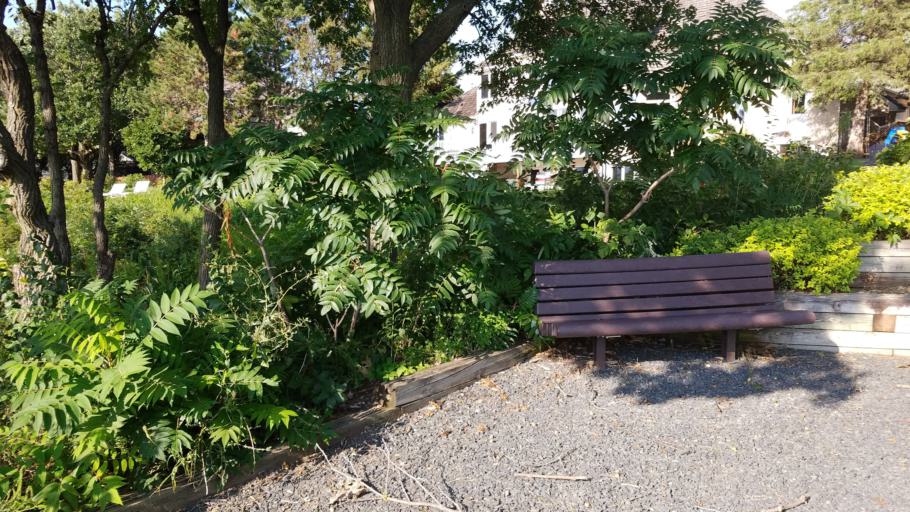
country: US
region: Minnesota
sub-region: Washington County
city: Lakeland
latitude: 44.9548
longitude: -92.7459
